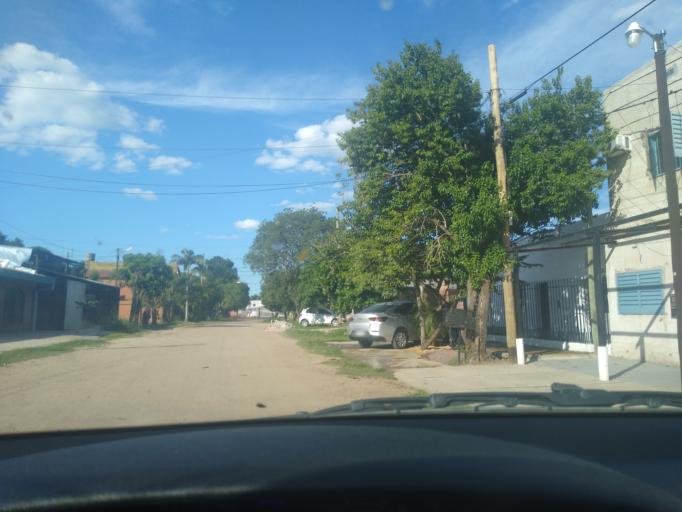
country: AR
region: Chaco
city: Barranqueras
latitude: -27.4793
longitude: -58.9286
